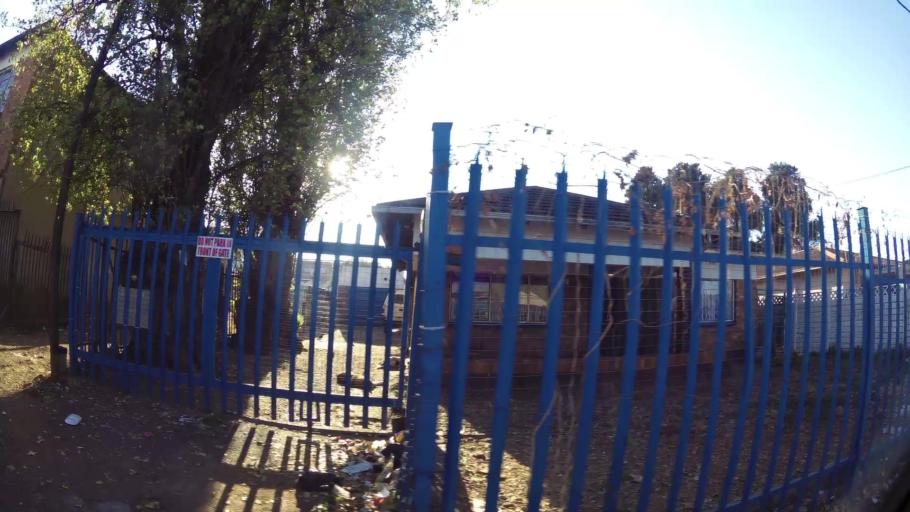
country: ZA
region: Gauteng
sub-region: Ekurhuleni Metropolitan Municipality
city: Germiston
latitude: -26.1973
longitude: 28.1477
